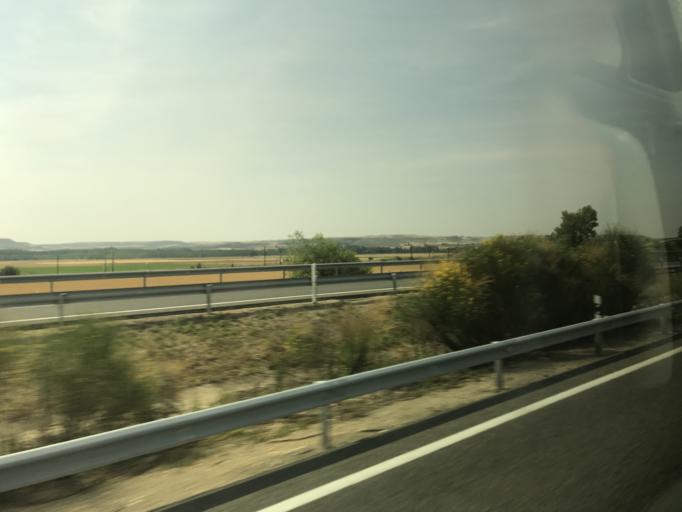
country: ES
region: Castille and Leon
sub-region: Provincia de Burgos
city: Villazopeque
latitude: 42.1902
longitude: -4.0343
